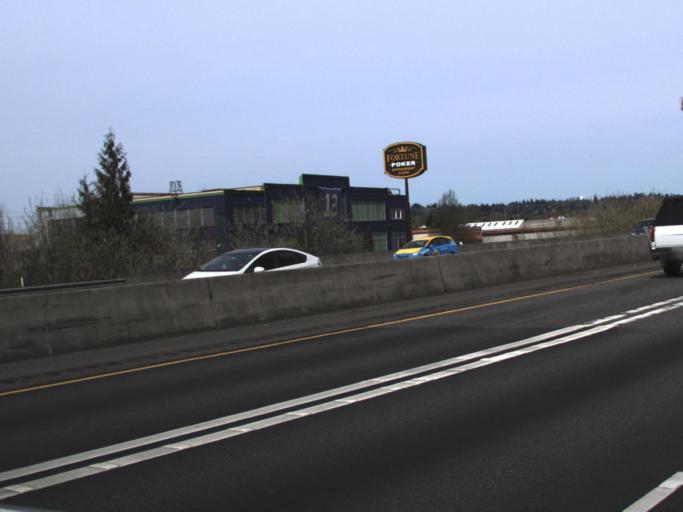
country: US
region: Washington
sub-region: King County
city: Renton
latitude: 47.4464
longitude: -122.2161
